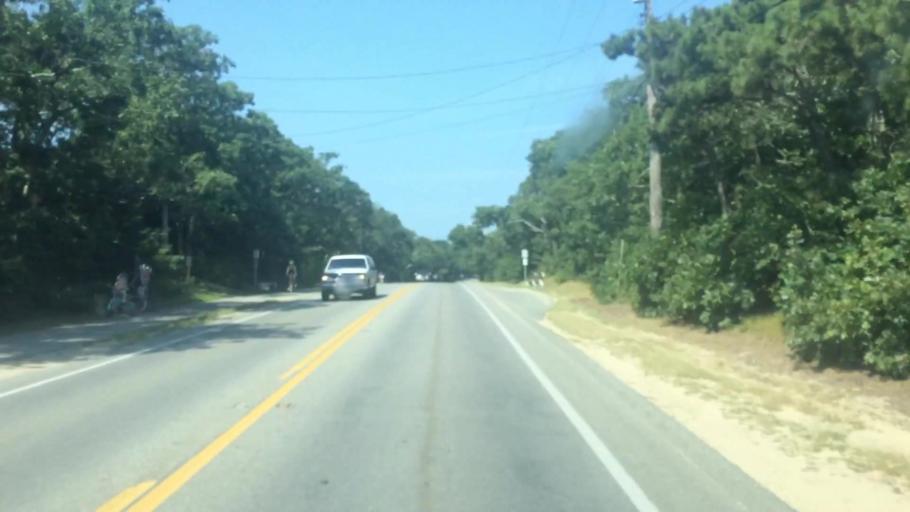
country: US
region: Massachusetts
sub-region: Dukes County
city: Edgartown
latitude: 41.3982
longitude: -70.5425
